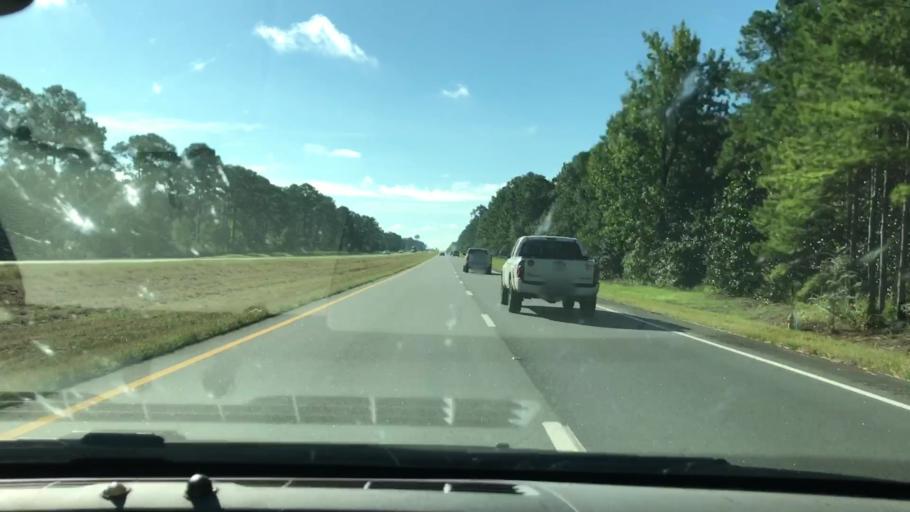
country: US
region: Georgia
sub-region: Lee County
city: Leesburg
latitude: 31.6537
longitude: -84.2679
